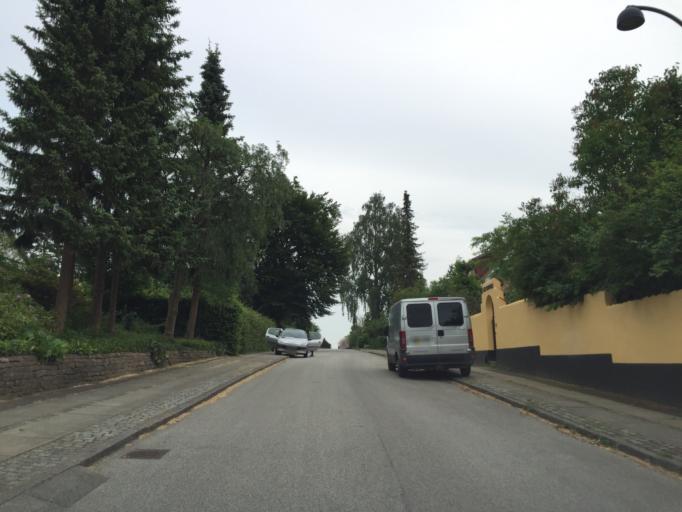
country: DK
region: Capital Region
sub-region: Lyngby-Tarbaek Kommune
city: Kongens Lyngby
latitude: 55.7677
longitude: 12.5278
